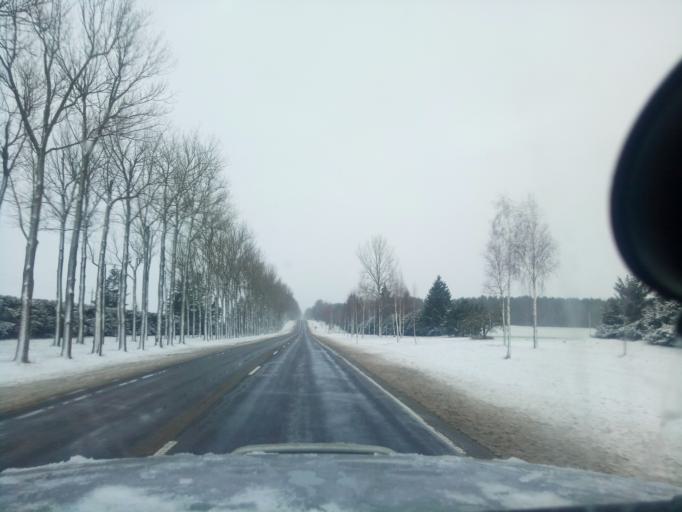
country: BY
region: Minsk
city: Haradzyeya
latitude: 53.3445
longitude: 26.5191
